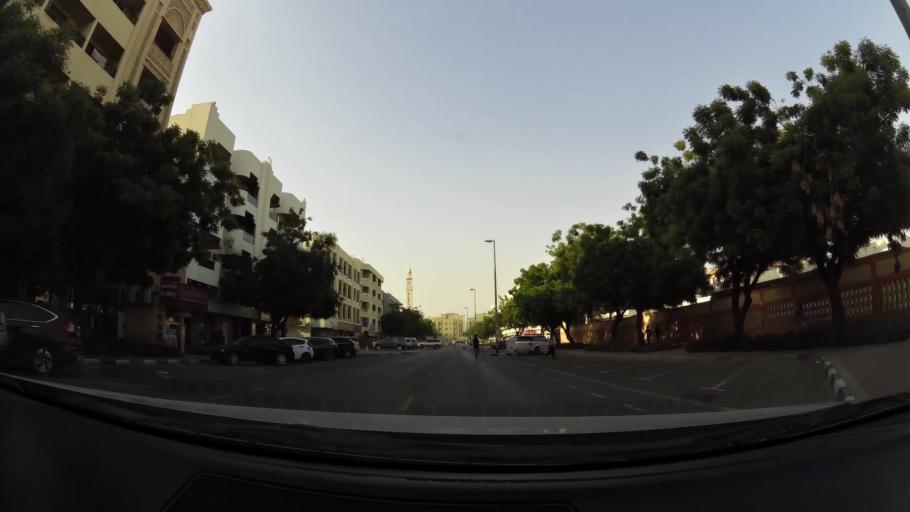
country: AE
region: Ash Shariqah
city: Sharjah
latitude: 25.2508
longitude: 55.3045
